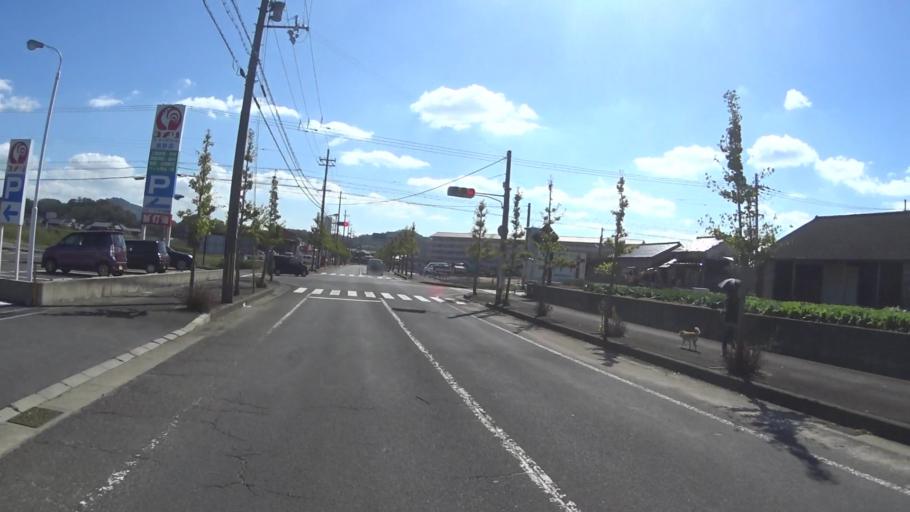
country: JP
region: Kyoto
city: Miyazu
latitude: 35.6797
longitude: 135.0230
